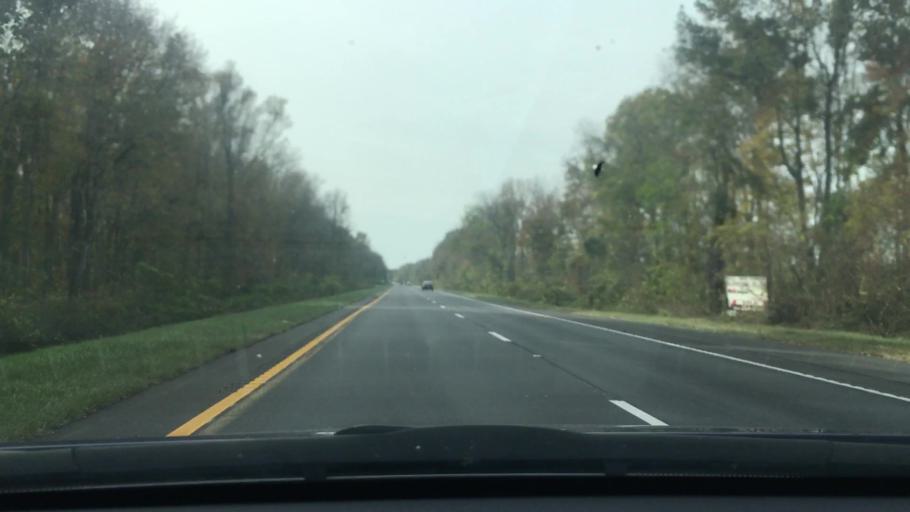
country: US
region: South Carolina
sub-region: Sumter County
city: Stateburg
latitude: 33.9495
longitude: -80.6115
